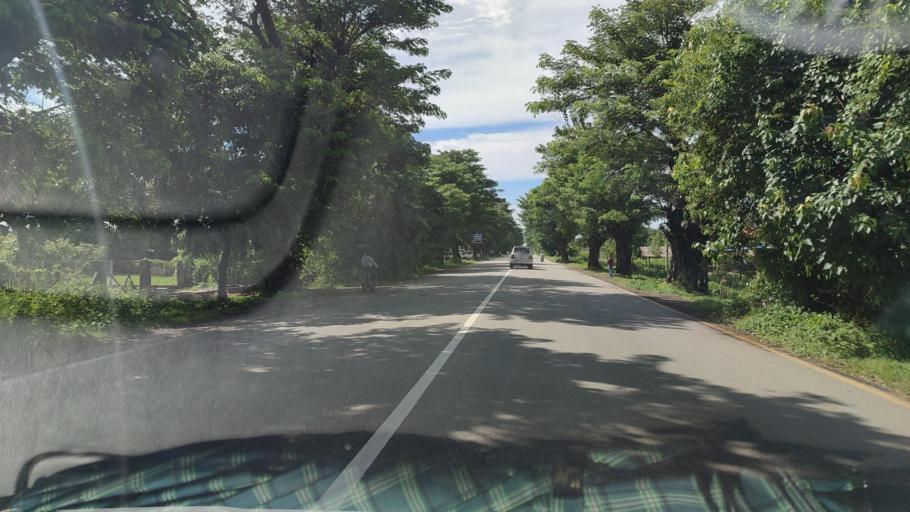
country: MM
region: Bago
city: Pyu
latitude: 18.2653
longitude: 96.5268
